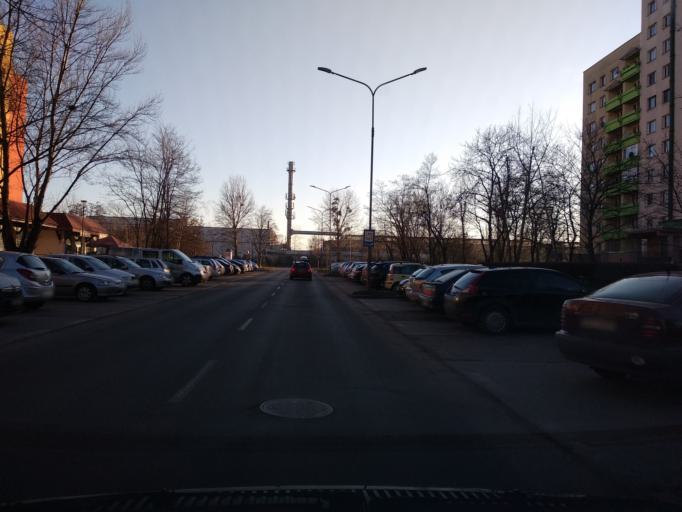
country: PL
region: Lower Silesian Voivodeship
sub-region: Powiat wroclawski
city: Wroclaw
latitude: 51.1230
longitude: 16.9671
